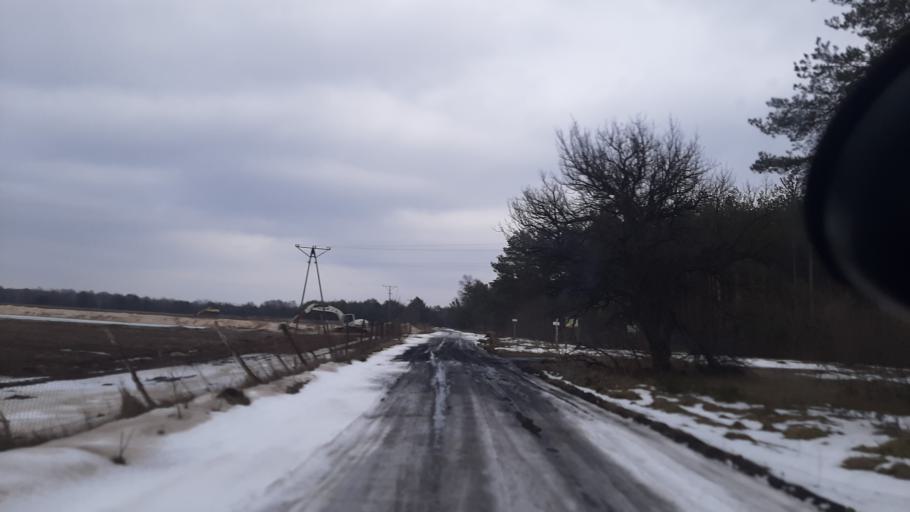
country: PL
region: Lublin Voivodeship
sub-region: Powiat wlodawski
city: Wlodawa
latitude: 51.5171
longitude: 23.5963
